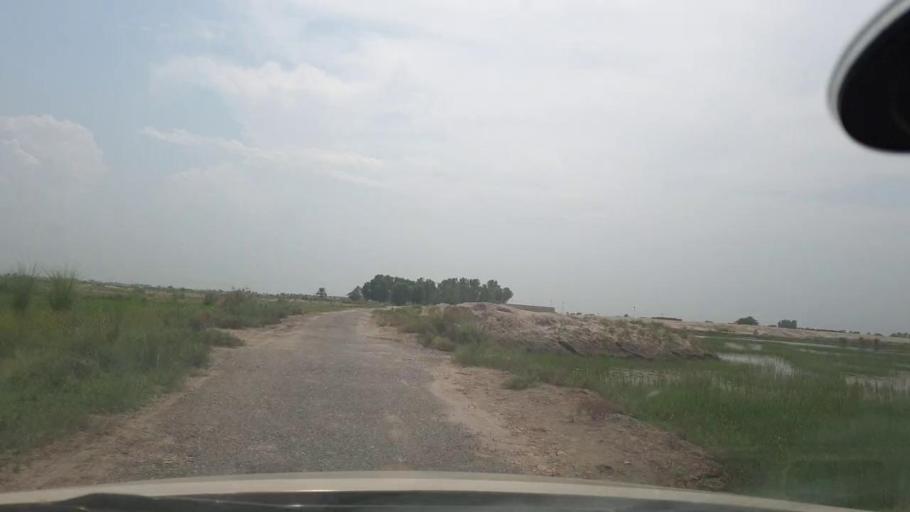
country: PK
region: Sindh
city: Jacobabad
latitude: 28.1415
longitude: 68.3543
